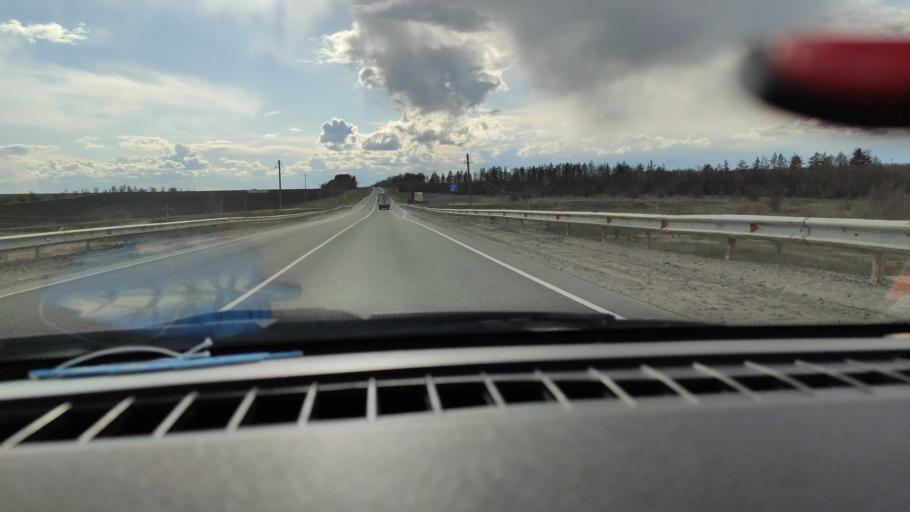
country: RU
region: Saratov
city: Sennoy
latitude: 52.1579
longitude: 47.0290
